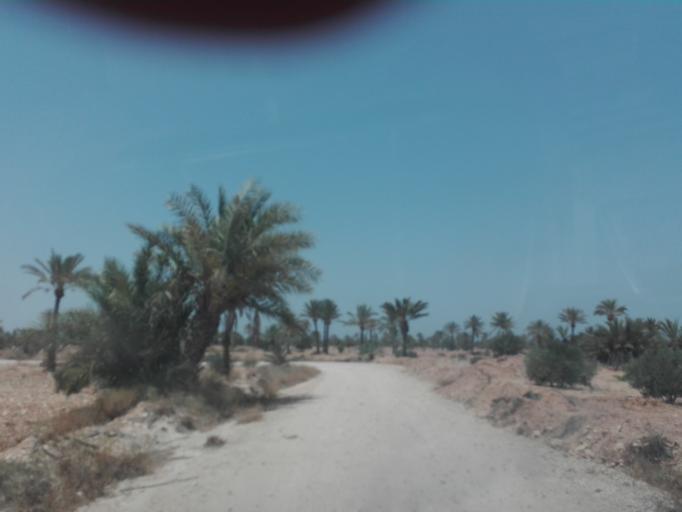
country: TN
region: Safaqis
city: Al Qarmadah
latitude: 34.6621
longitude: 11.0946
